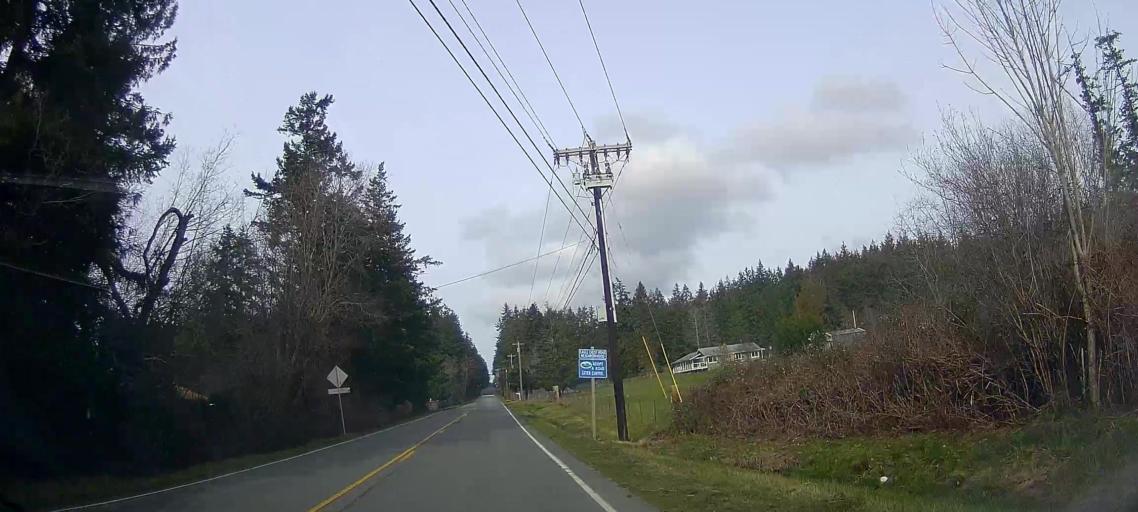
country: US
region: Washington
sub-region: Island County
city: Camano
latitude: 48.1829
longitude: -122.5273
